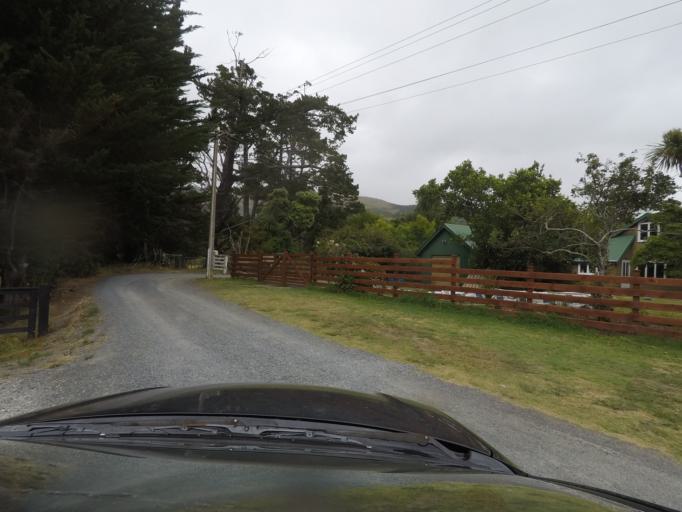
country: NZ
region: Auckland
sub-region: Auckland
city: Warkworth
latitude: -36.2662
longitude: 174.7280
